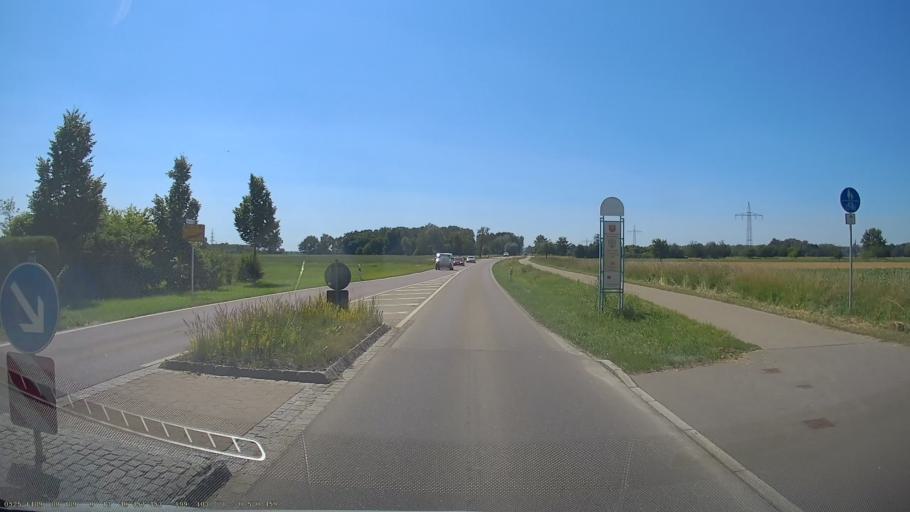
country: DE
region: Bavaria
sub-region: Swabia
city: Holzheim
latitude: 48.3867
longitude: 10.0725
